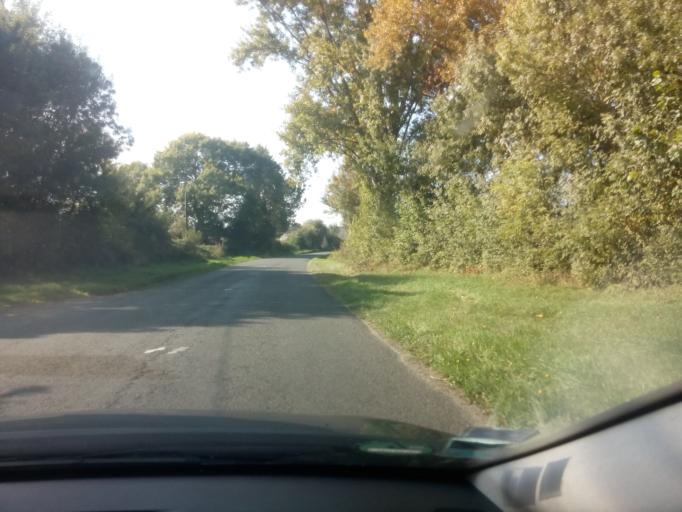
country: FR
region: Pays de la Loire
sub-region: Departement de Maine-et-Loire
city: Soulaire-et-Bourg
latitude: 47.5753
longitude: -0.5337
